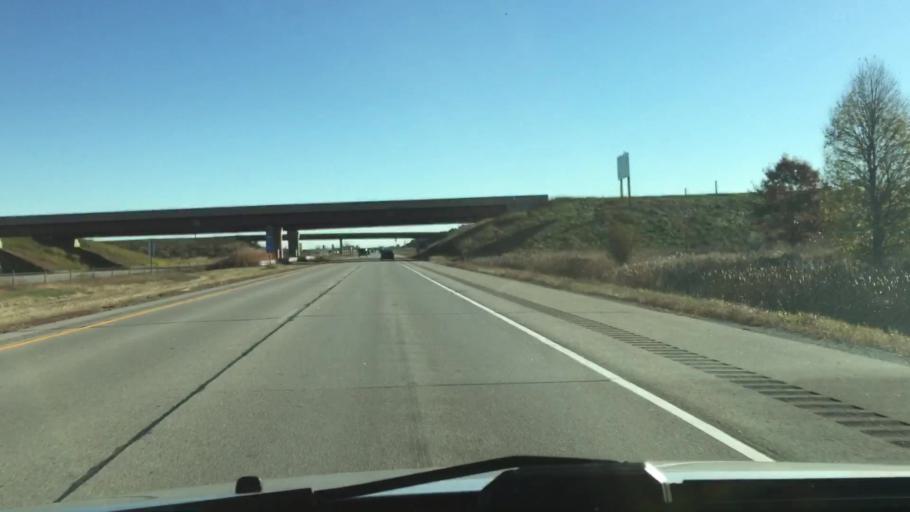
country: US
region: Wisconsin
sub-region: Outagamie County
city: Kimberly
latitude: 44.2979
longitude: -88.3576
